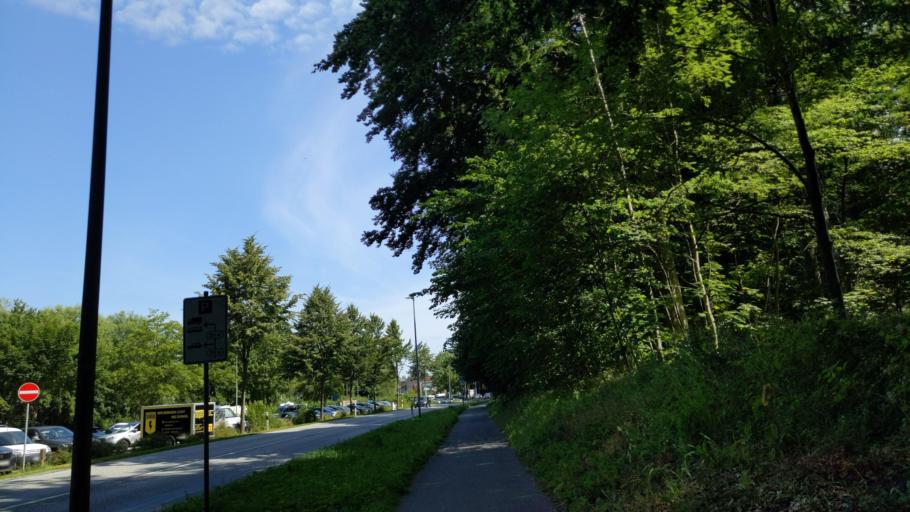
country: DE
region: Schleswig-Holstein
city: Ploen
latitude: 54.1519
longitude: 10.4032
